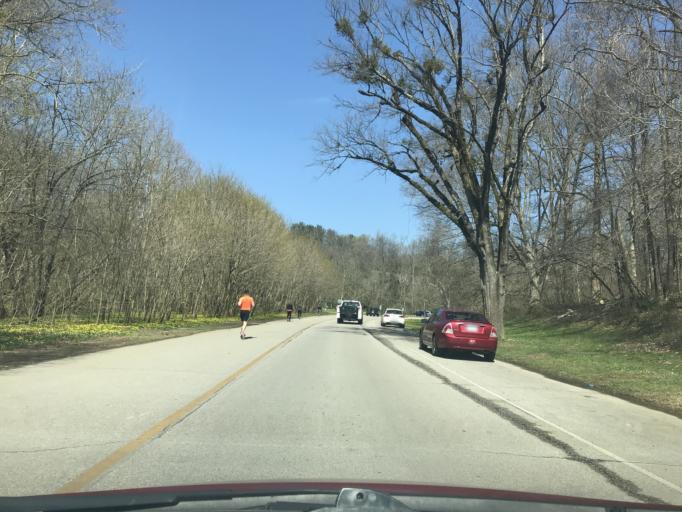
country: US
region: Kentucky
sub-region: Jefferson County
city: Saint Matthews
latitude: 38.2403
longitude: -85.6947
